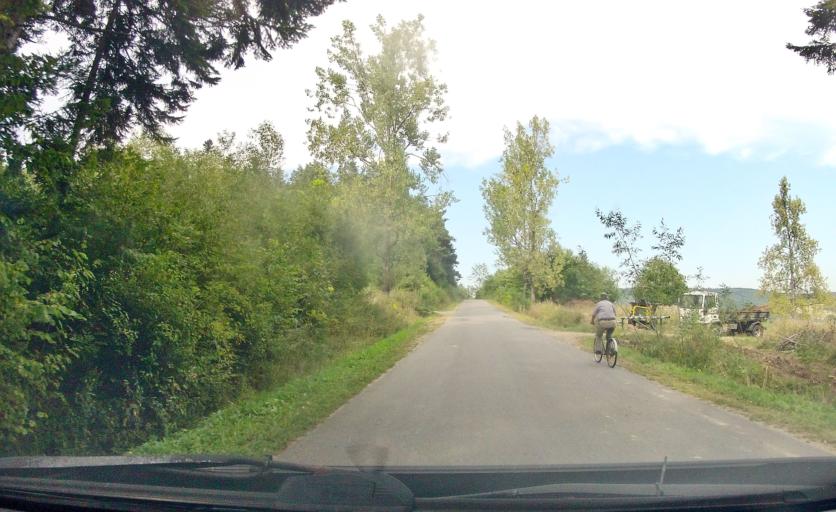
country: PL
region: Subcarpathian Voivodeship
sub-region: Powiat krosnienski
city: Dukla
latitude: 49.5031
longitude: 21.6227
